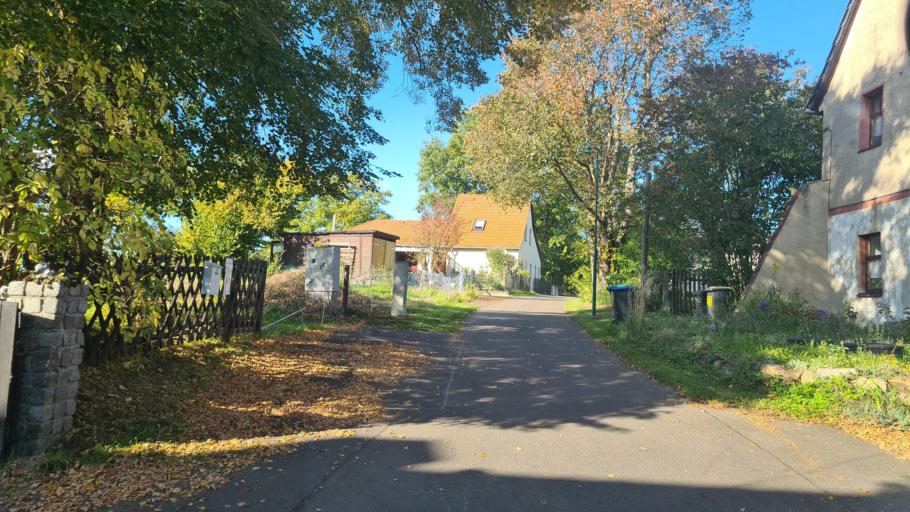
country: DE
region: Saxony
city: Borna
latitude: 51.1512
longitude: 12.4886
